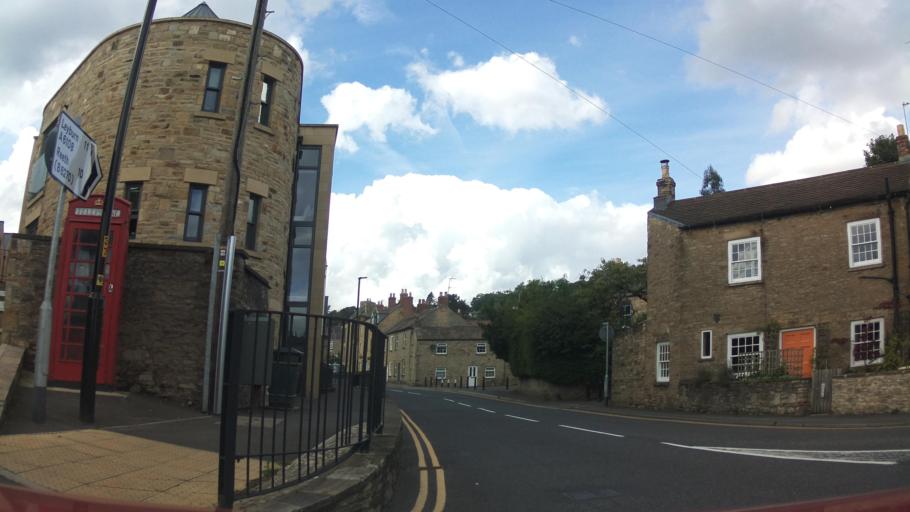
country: GB
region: England
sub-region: North Yorkshire
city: Catterick Garrison
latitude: 54.4046
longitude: -1.7437
